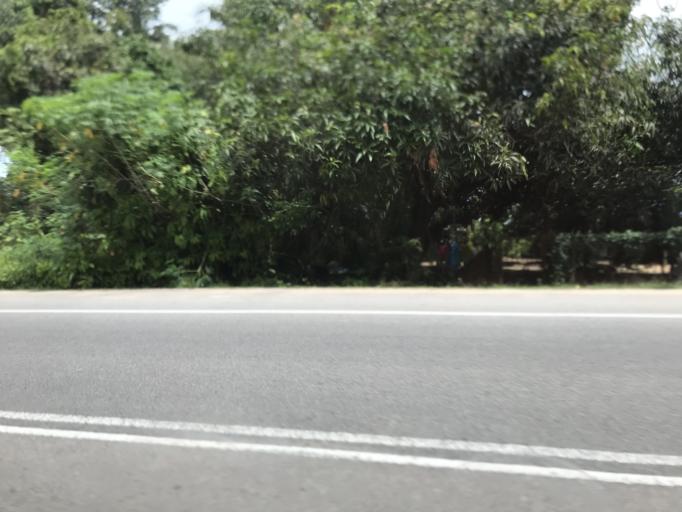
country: MY
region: Kelantan
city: Tumpat
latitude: 6.1730
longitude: 102.1841
